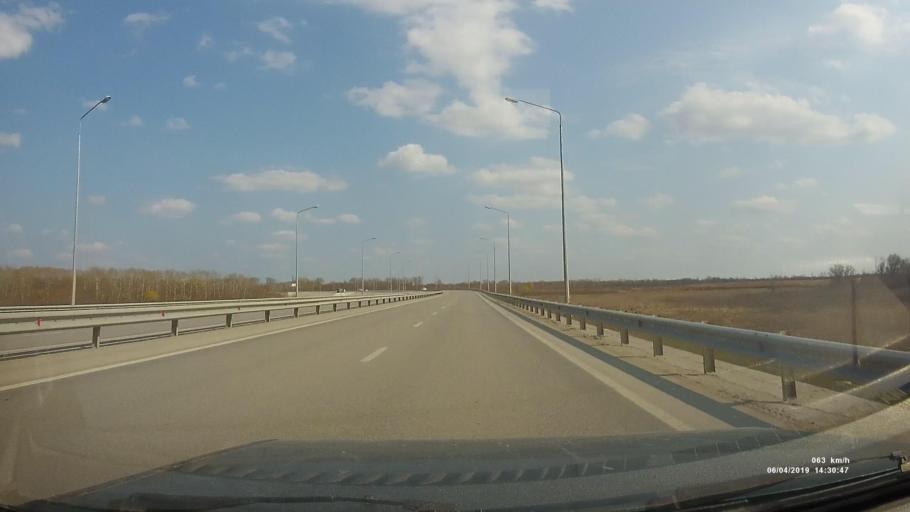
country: RU
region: Rostov
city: Rostov-na-Donu
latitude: 47.2062
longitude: 39.7516
